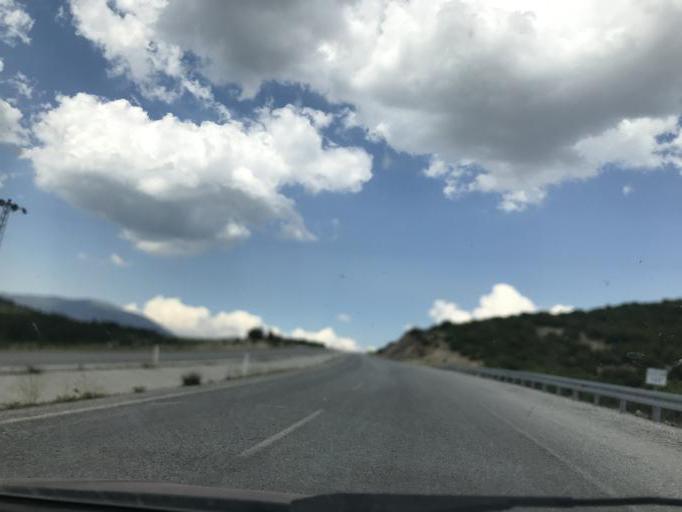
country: TR
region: Denizli
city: Tavas
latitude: 37.5839
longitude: 29.1011
